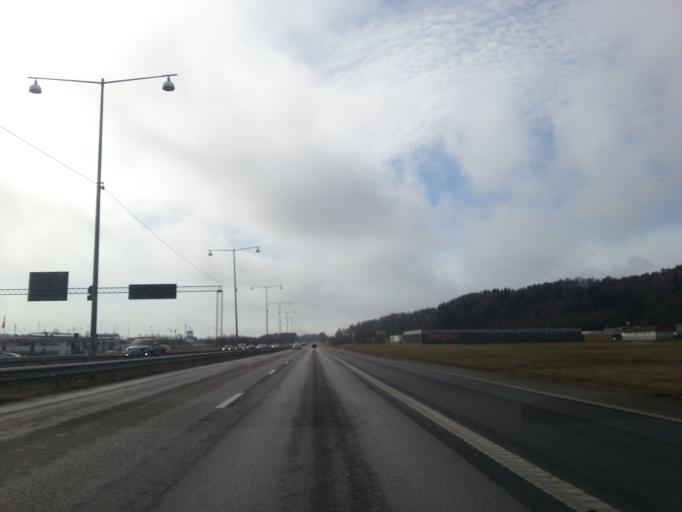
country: SE
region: Vaestra Goetaland
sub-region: Goteborg
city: Hammarkullen
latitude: 57.7726
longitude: 11.9965
